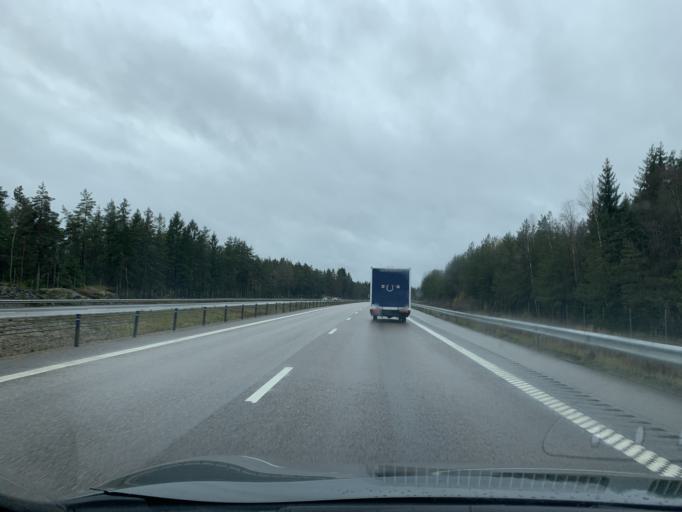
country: SE
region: Stockholm
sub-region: Sodertalje Kommun
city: Molnbo
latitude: 58.9238
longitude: 17.3896
